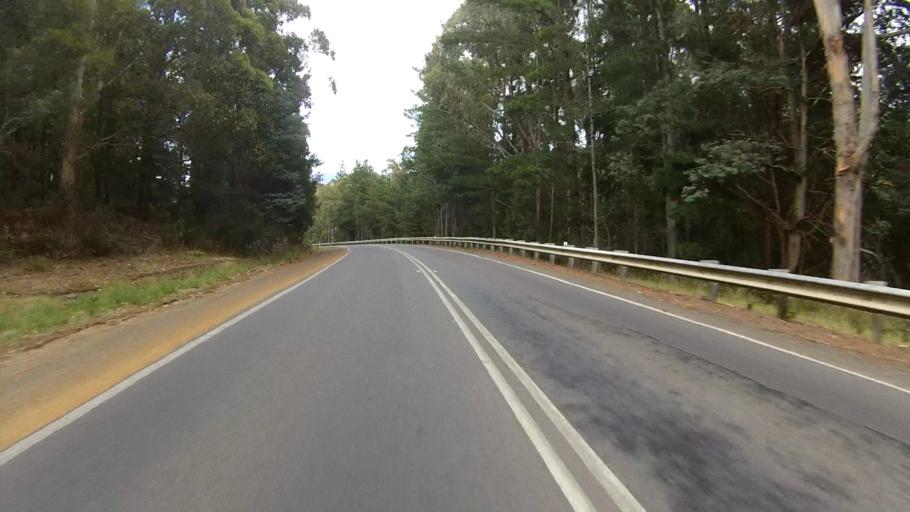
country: AU
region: Tasmania
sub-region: Kingborough
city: Kettering
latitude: -43.0953
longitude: 147.2434
